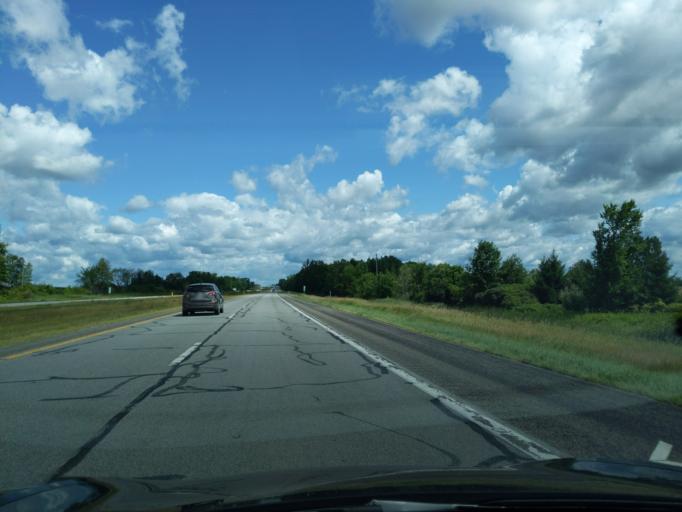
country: US
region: Michigan
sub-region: Clare County
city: Clare
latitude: 43.7697
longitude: -84.7585
